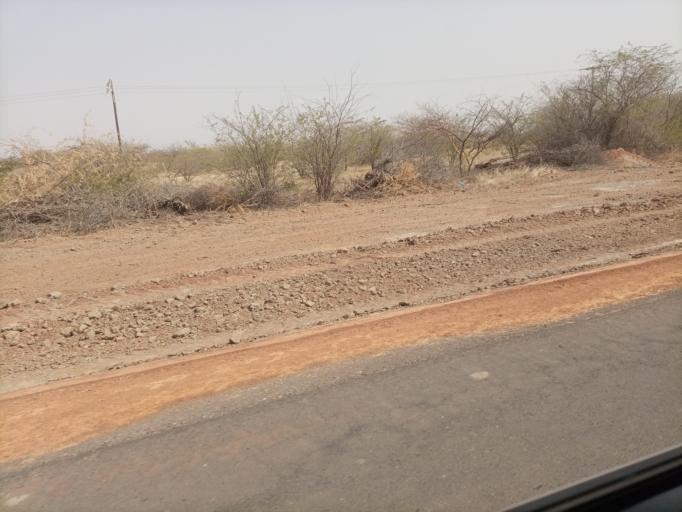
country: SN
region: Fatick
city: Foundiougne
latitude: 14.1584
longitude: -16.4683
